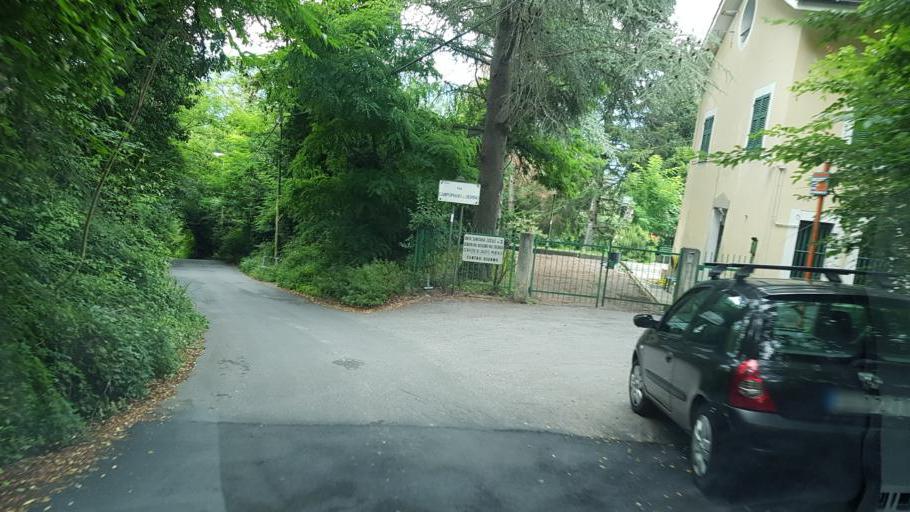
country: IT
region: Liguria
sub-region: Provincia di Genova
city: Piccarello
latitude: 44.4404
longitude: 9.0055
